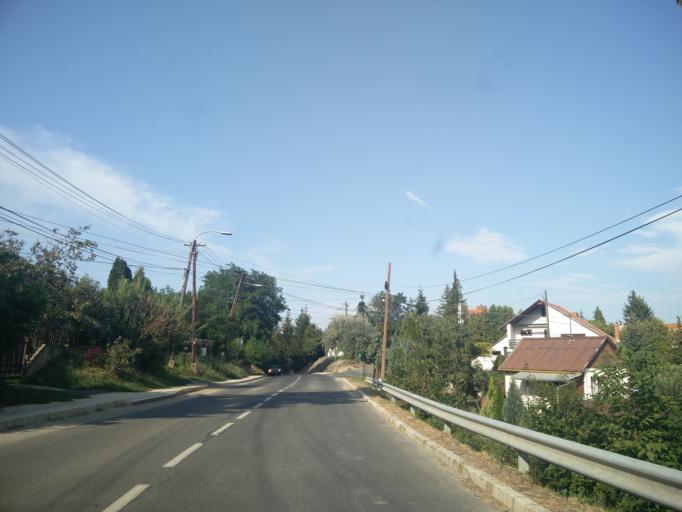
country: HU
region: Zala
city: Zalaegerszeg
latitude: 46.8261
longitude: 16.8222
